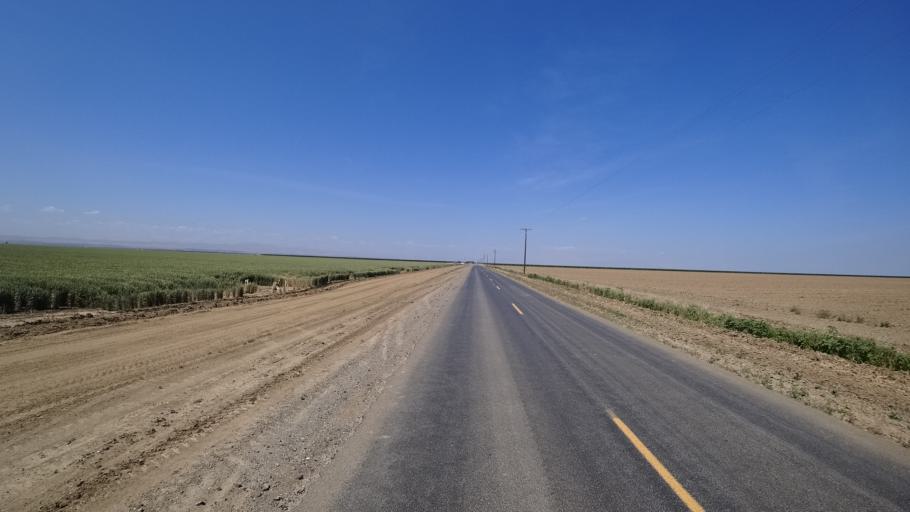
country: US
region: California
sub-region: Kings County
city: Kettleman City
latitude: 36.1377
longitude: -119.9453
